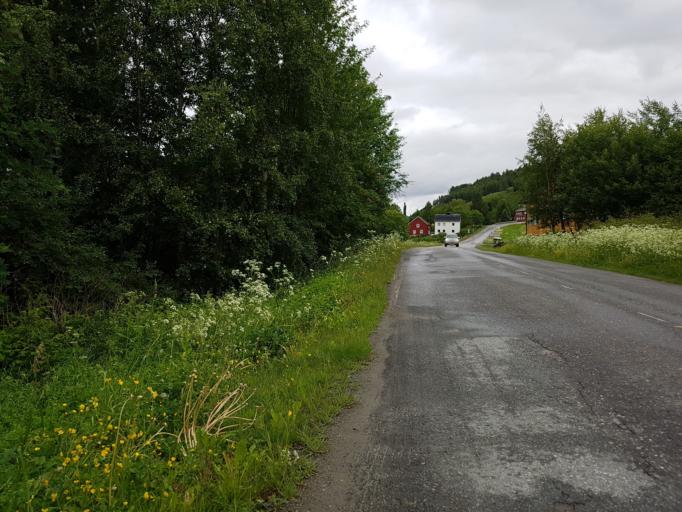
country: NO
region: Sor-Trondelag
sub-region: Selbu
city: Mebonden
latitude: 63.2311
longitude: 11.0323
